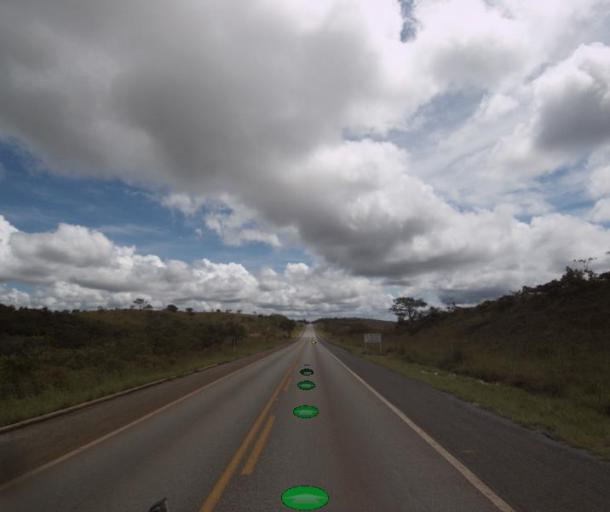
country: BR
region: Goias
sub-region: Abadiania
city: Abadiania
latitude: -15.7821
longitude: -48.4895
